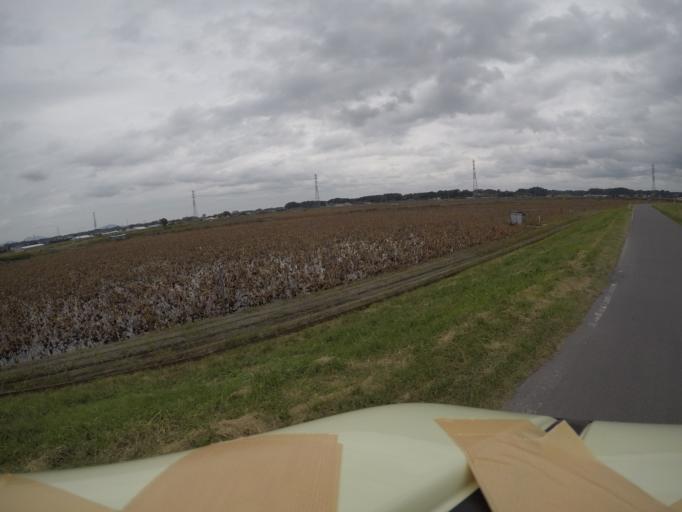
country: JP
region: Ibaraki
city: Ishioka
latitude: 36.1493
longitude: 140.3585
